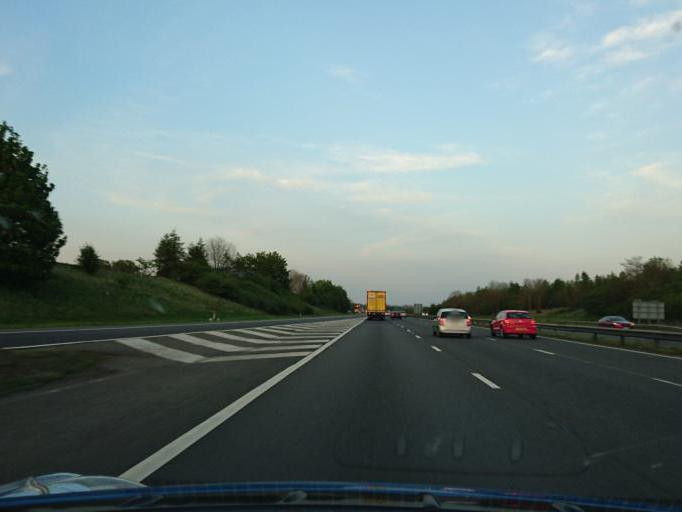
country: GB
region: England
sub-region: Warwickshire
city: Rugby
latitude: 52.4078
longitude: -1.2419
